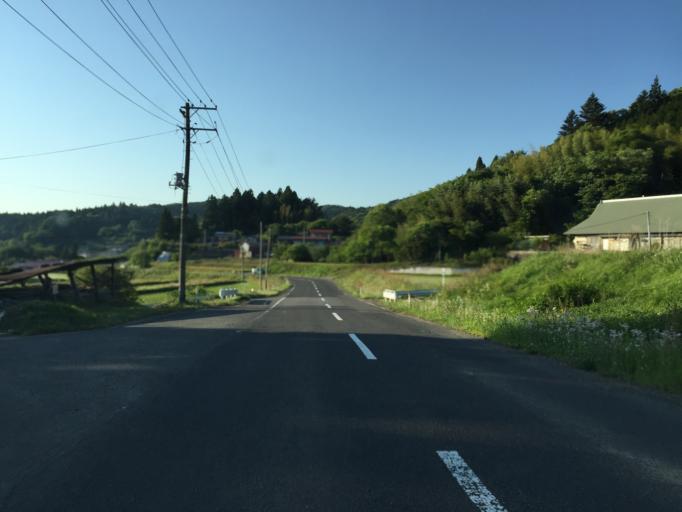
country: JP
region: Fukushima
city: Ishikawa
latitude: 37.0388
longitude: 140.4357
